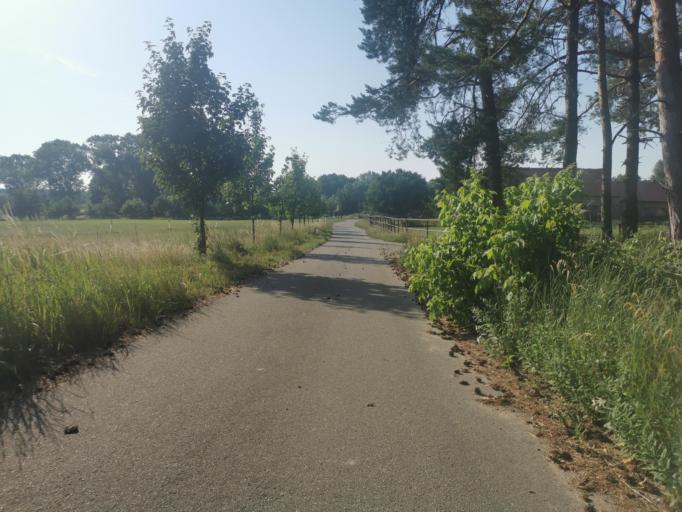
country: CZ
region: South Moravian
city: Ratiskovice
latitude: 48.9229
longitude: 17.1977
